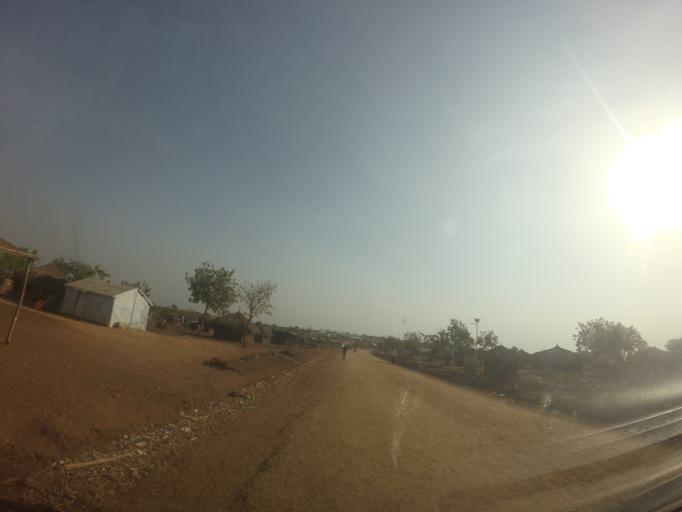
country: UG
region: Northern Region
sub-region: Maracha District
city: Maracha
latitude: 3.1252
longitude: 31.1602
